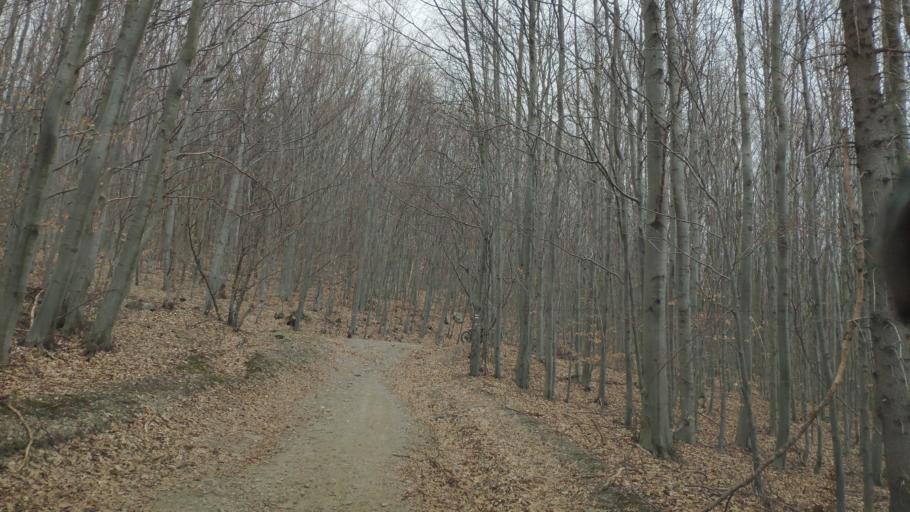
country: SK
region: Kosicky
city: Gelnica
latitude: 48.7561
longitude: 21.0215
